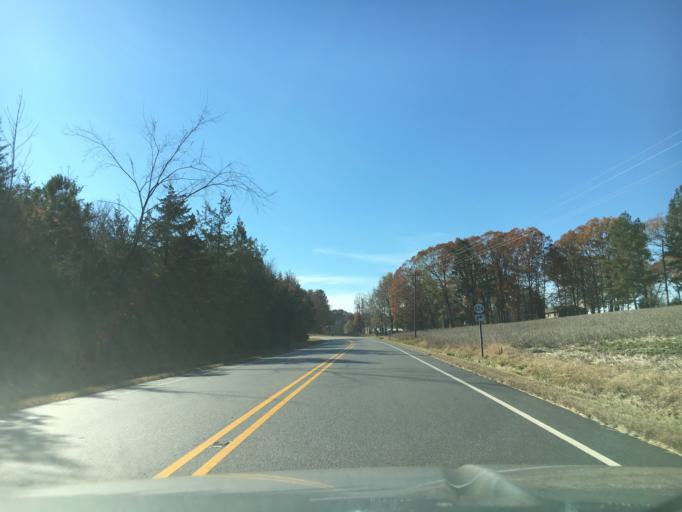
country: US
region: Virginia
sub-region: Cumberland County
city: Cumberland
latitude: 37.5258
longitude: -78.2053
